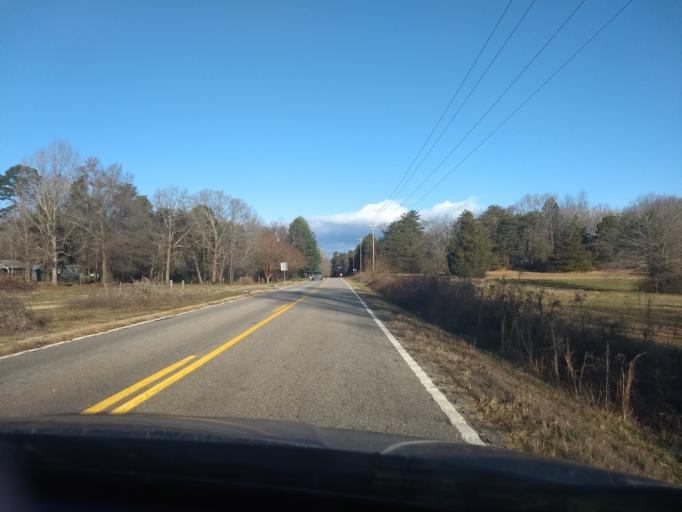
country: US
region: South Carolina
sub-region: Greenville County
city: Greer
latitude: 35.0046
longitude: -82.2148
